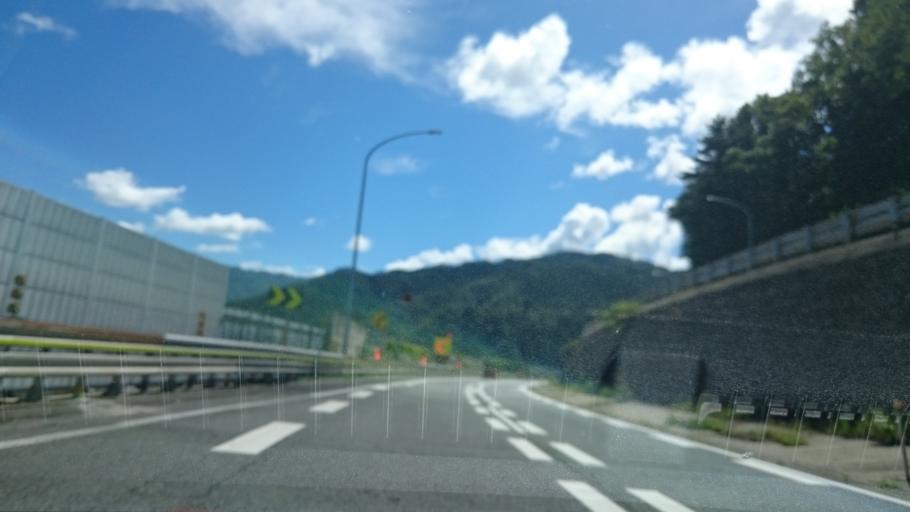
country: JP
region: Nagano
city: Iida
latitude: 35.4475
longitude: 137.7448
